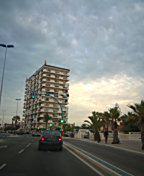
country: ES
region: Murcia
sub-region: Murcia
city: La Manga del Mar Menor
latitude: 37.6874
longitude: -0.7368
